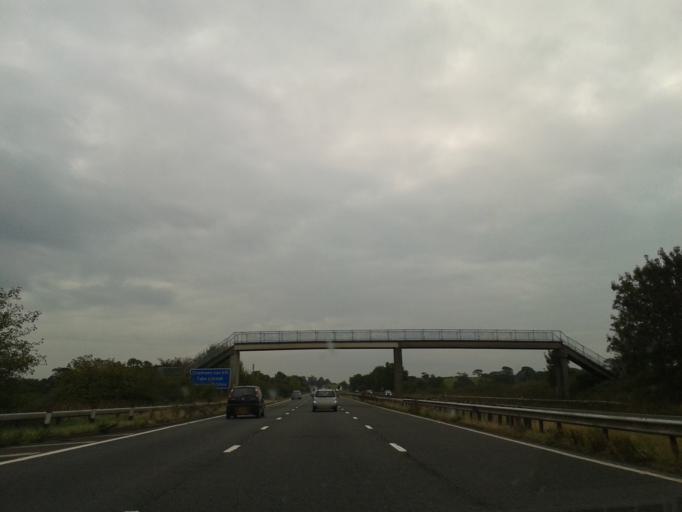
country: GB
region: England
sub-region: Lancashire
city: Galgate
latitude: 53.9942
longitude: -2.7806
